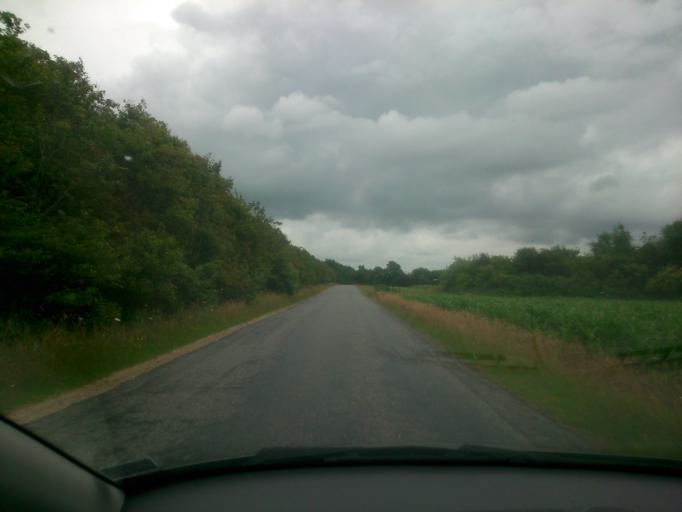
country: DK
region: South Denmark
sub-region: Varde Kommune
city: Varde
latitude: 55.5544
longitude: 8.4477
